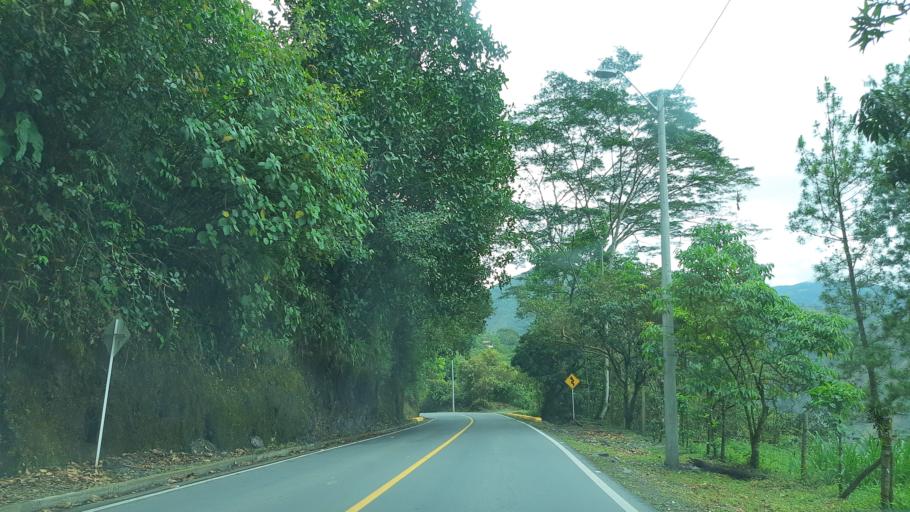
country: CO
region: Boyaca
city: Chivor
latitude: 4.9402
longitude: -73.3069
